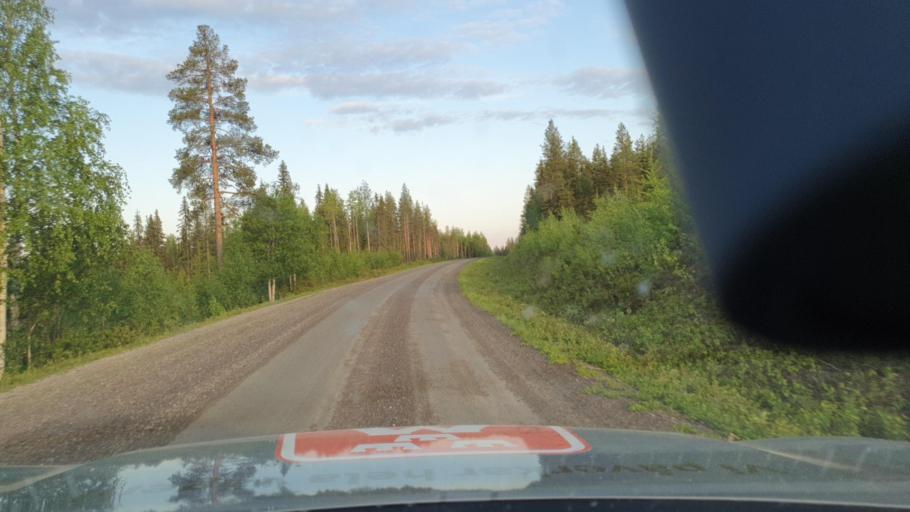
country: SE
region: Norrbotten
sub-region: Bodens Kommun
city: Boden
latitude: 66.4662
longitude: 21.6370
